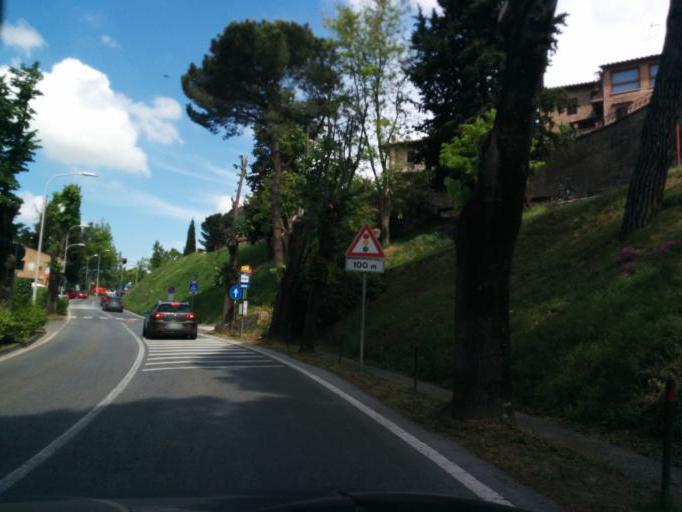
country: IT
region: Tuscany
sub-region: Provincia di Siena
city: San Gimignano
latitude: 43.4663
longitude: 11.0415
